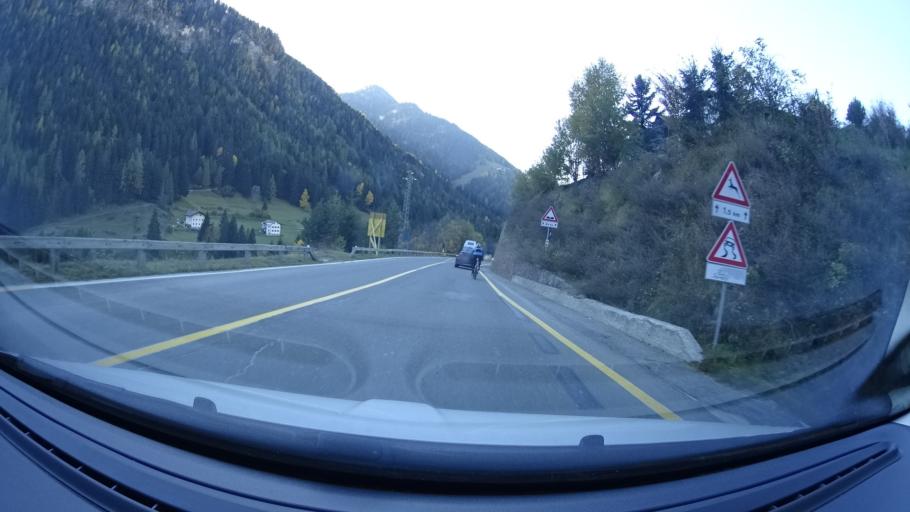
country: IT
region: Trentino-Alto Adige
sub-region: Bolzano
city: Ortisei
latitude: 46.5640
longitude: 11.6985
